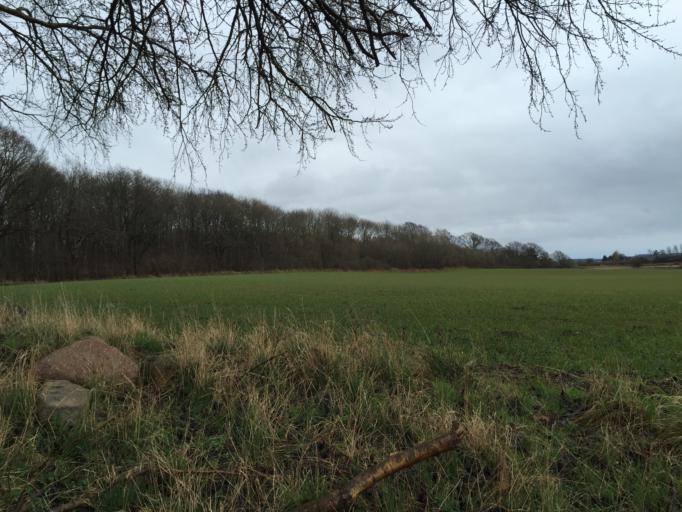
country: DK
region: South Denmark
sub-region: Assens Kommune
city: Harby
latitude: 55.1386
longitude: 10.0311
